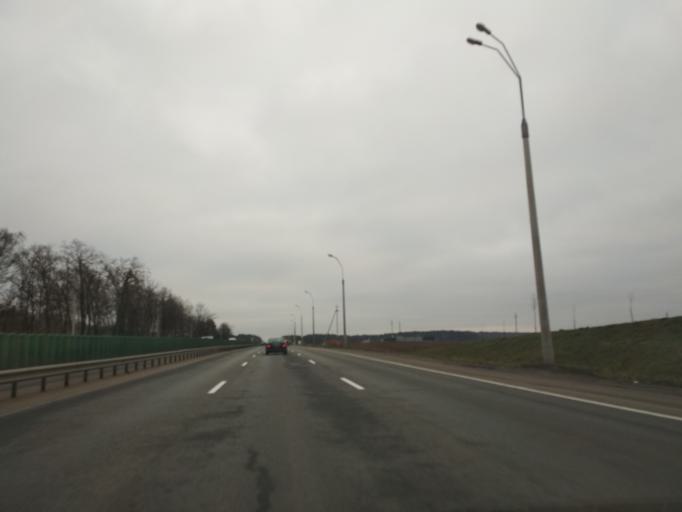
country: BY
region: Minsk
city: Vyaliki Trastsyanets
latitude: 53.8368
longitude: 27.7290
